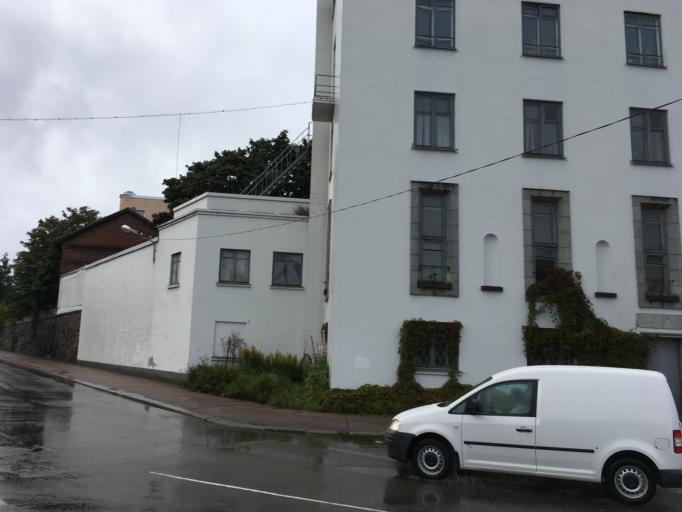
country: RU
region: Leningrad
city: Vyborg
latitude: 60.7088
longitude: 28.7382
